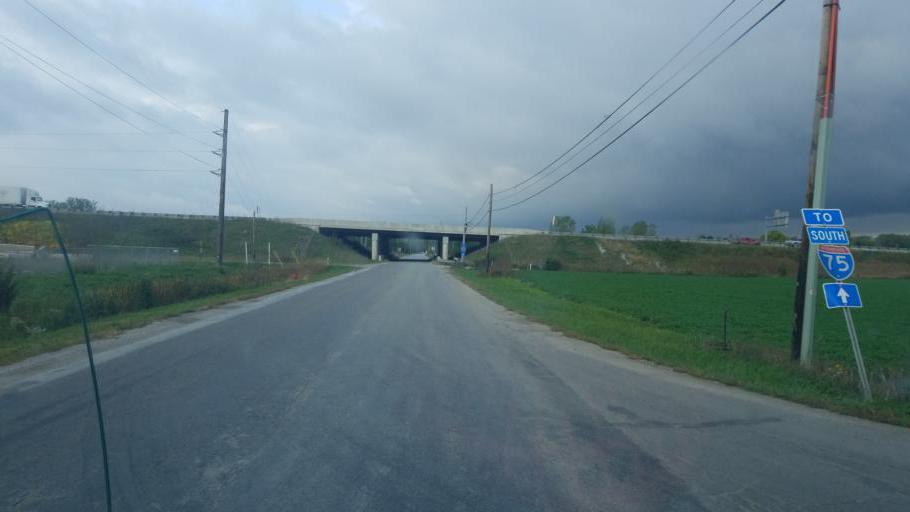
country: US
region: Ohio
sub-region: Wood County
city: North Baltimore
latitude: 41.1823
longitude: -83.6478
